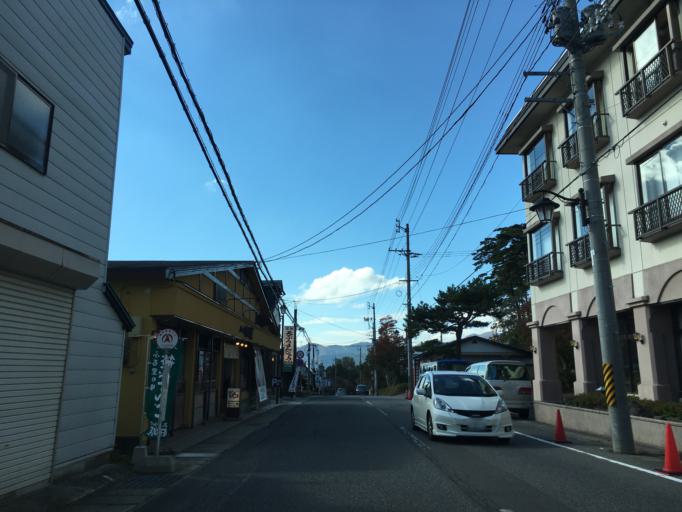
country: JP
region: Fukushima
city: Inawashiro
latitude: 37.6148
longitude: 140.2089
